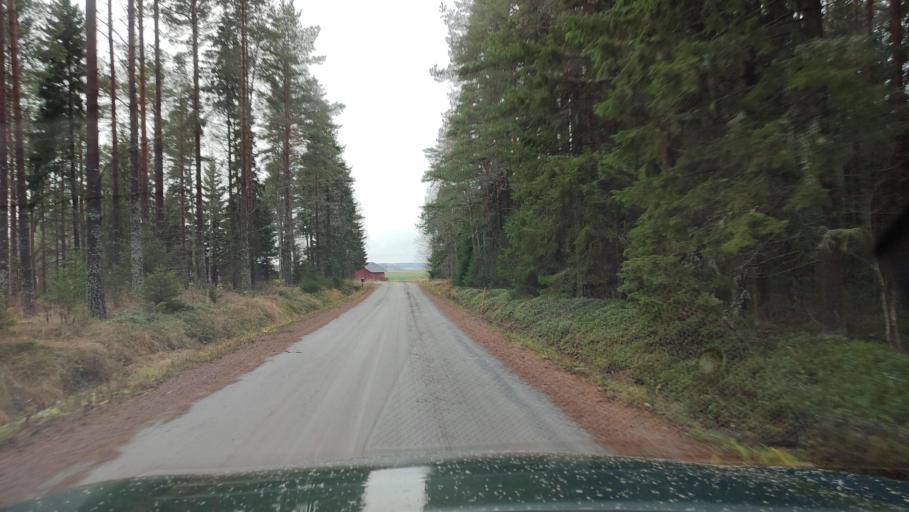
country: FI
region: Ostrobothnia
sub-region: Sydosterbotten
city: Naerpes
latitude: 62.4522
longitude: 21.4591
